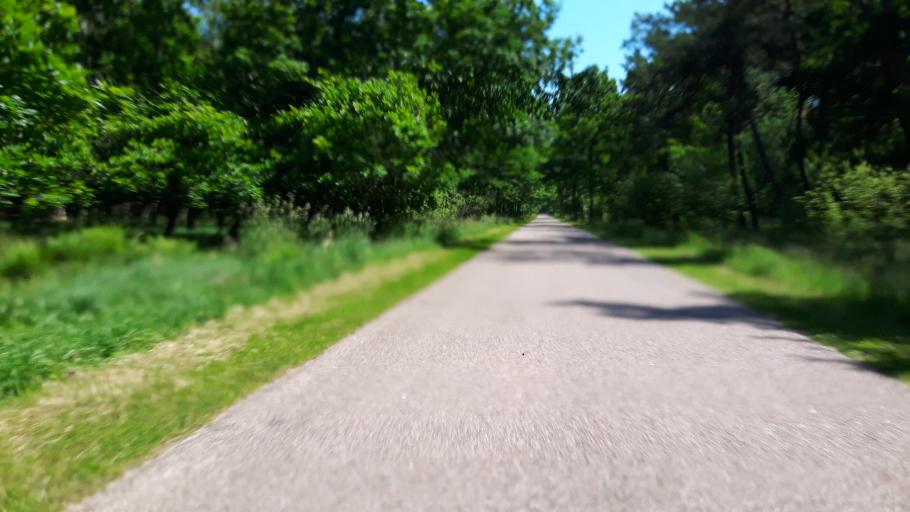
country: PL
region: Pomeranian Voivodeship
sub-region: Powiat slupski
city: Glowczyce
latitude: 54.6829
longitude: 17.3118
